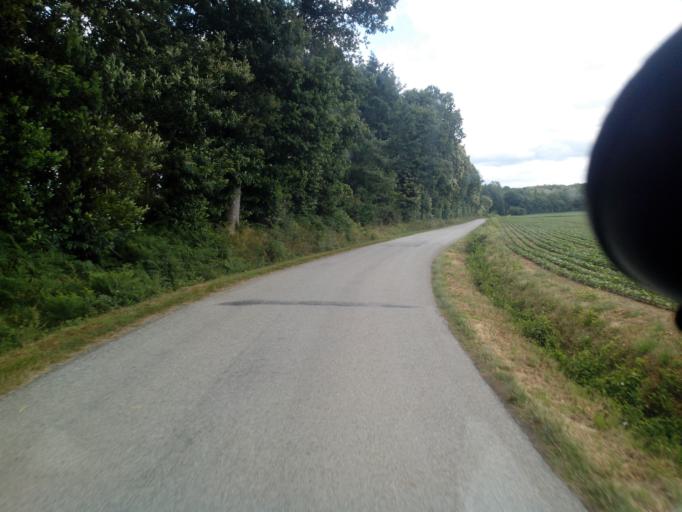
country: FR
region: Brittany
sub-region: Departement du Morbihan
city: Meneac
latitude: 48.1298
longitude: -2.4500
